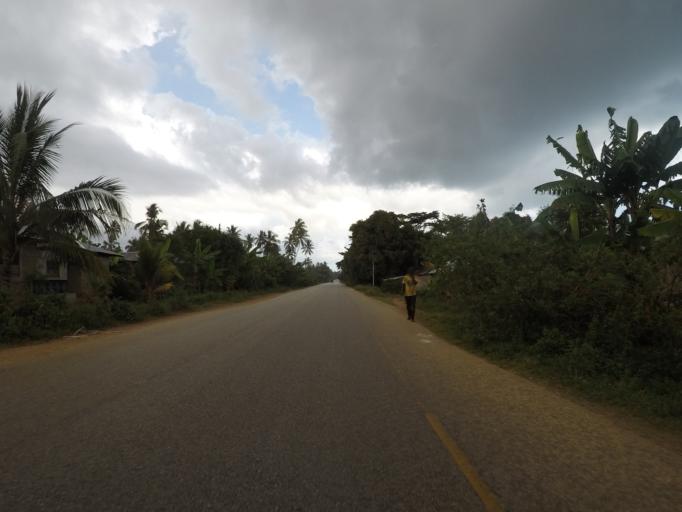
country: TZ
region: Zanzibar North
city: Mkokotoni
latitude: -5.9774
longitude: 39.1961
